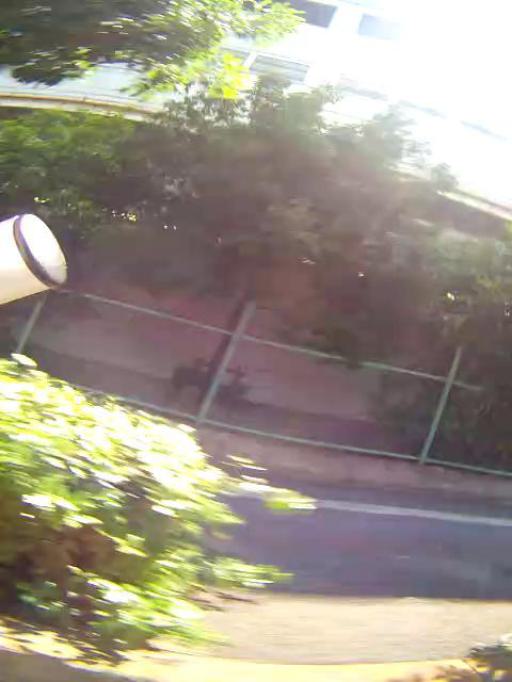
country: JP
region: Osaka
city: Matsubara
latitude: 34.6026
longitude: 135.5504
